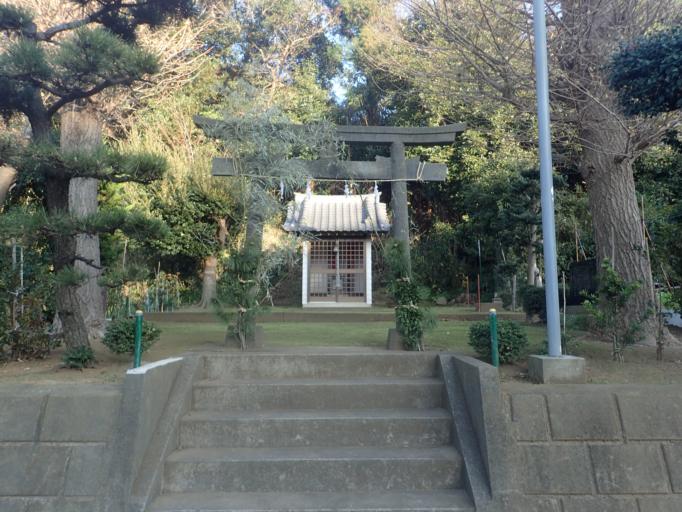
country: JP
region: Kanagawa
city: Miura
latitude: 35.2064
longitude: 139.6155
